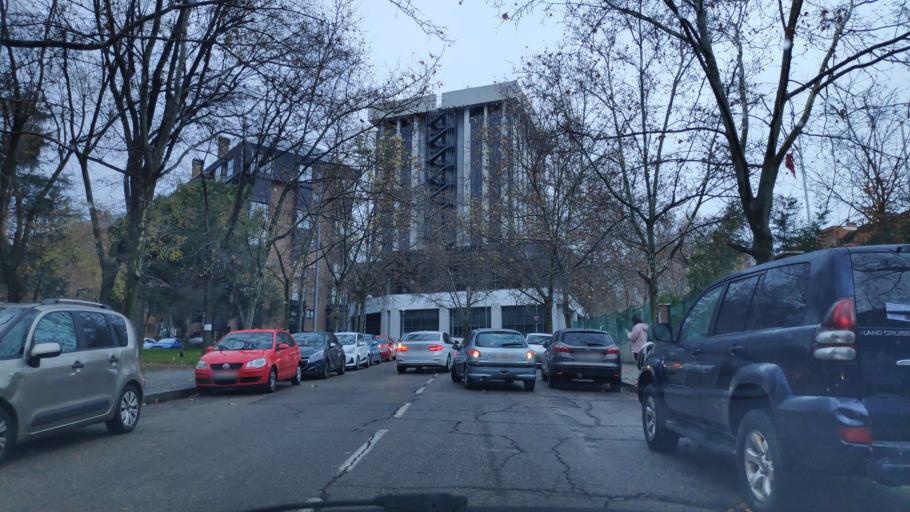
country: ES
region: Madrid
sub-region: Provincia de Madrid
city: Pinar de Chamartin
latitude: 40.4820
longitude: -3.6669
